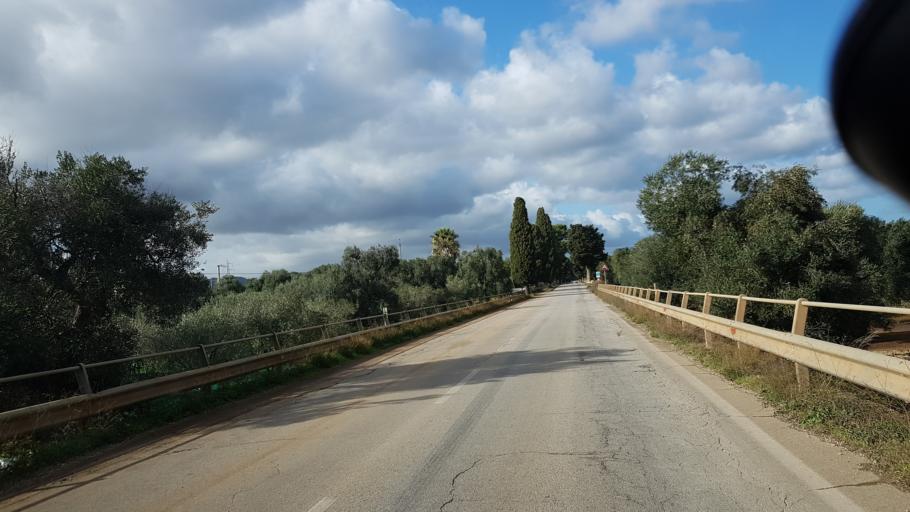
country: IT
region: Apulia
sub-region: Provincia di Brindisi
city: Ostuni
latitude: 40.7539
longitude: 17.5437
